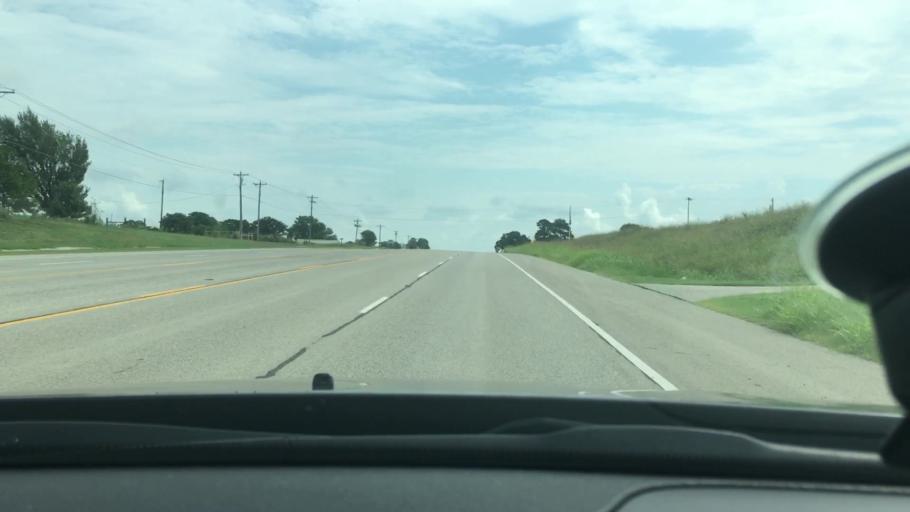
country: US
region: Oklahoma
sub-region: Carter County
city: Dickson
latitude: 34.1871
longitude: -97.0007
